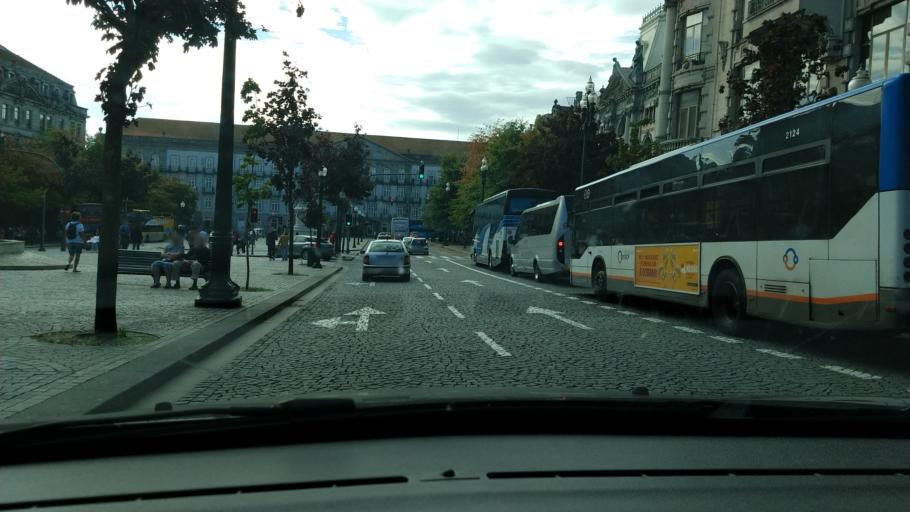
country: PT
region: Porto
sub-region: Porto
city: Porto
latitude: 41.1474
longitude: -8.6113
